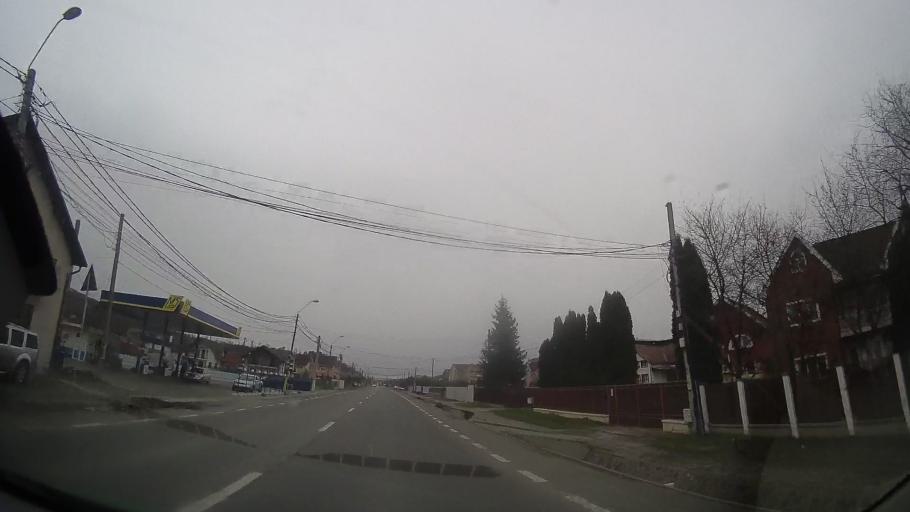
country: RO
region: Mures
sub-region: Comuna Santana de Mures
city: Santana de Mures
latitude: 46.5885
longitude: 24.5361
